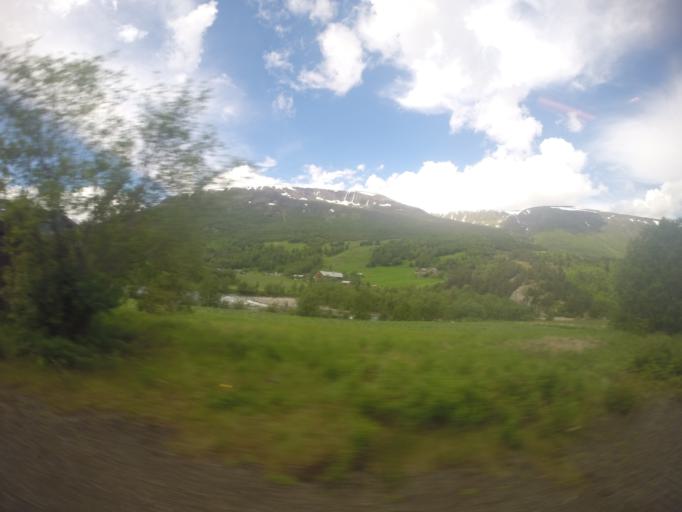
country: NO
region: Sor-Trondelag
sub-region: Oppdal
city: Oppdal
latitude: 62.5141
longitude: 9.6034
